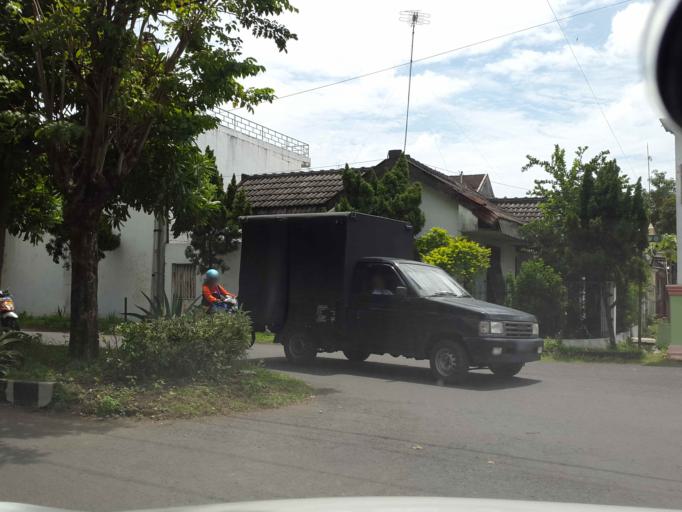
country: ID
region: East Java
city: Mojokerto
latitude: -7.4629
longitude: 112.4441
